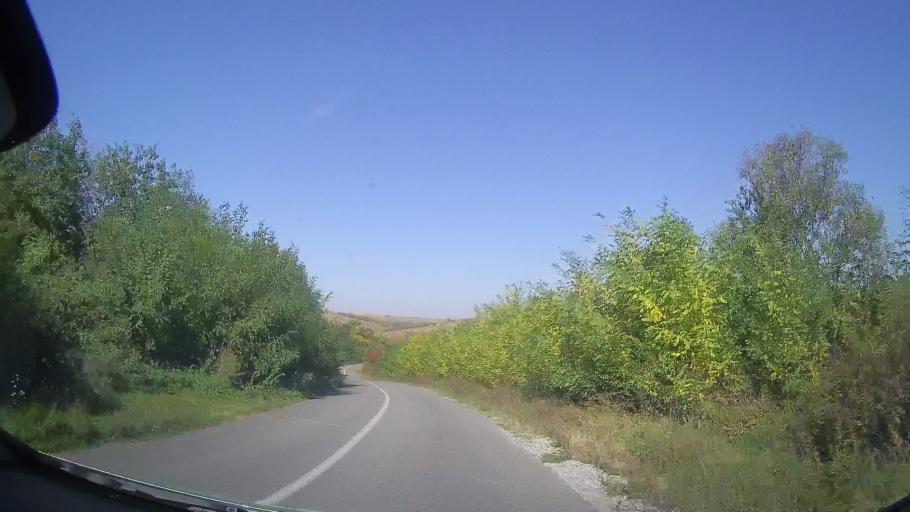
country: RO
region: Timis
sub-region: Comuna Balint
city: Balint
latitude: 45.8370
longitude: 21.8563
